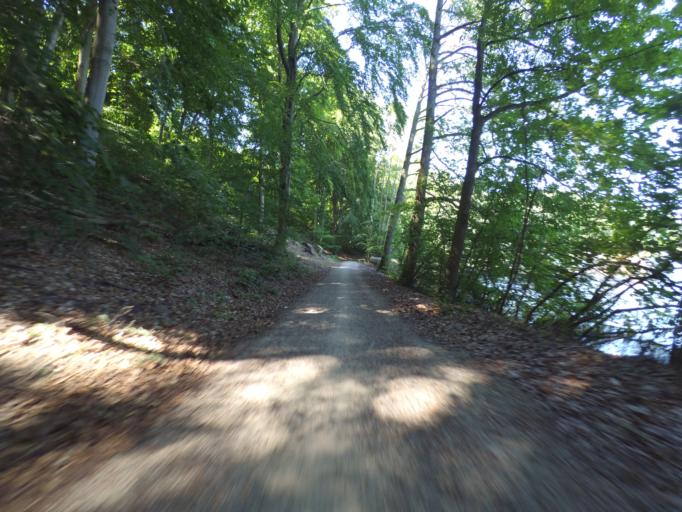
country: DE
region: Mecklenburg-Vorpommern
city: Plau am See
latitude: 53.3920
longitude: 12.3098
